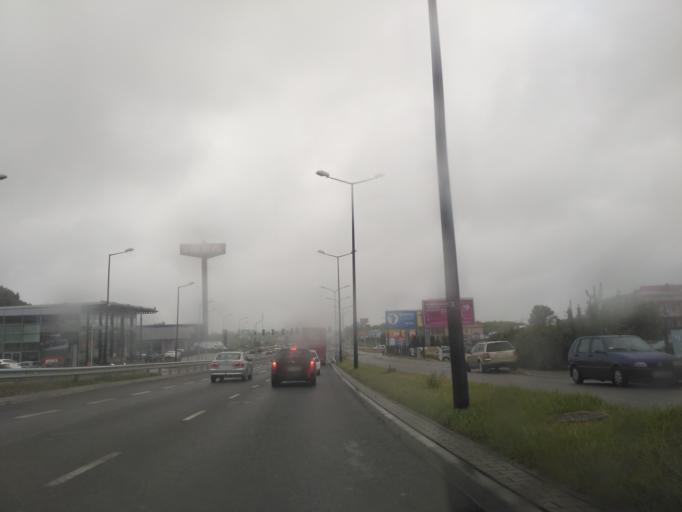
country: PL
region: Lublin Voivodeship
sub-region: Powiat lubelski
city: Lublin
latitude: 51.2787
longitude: 22.5743
